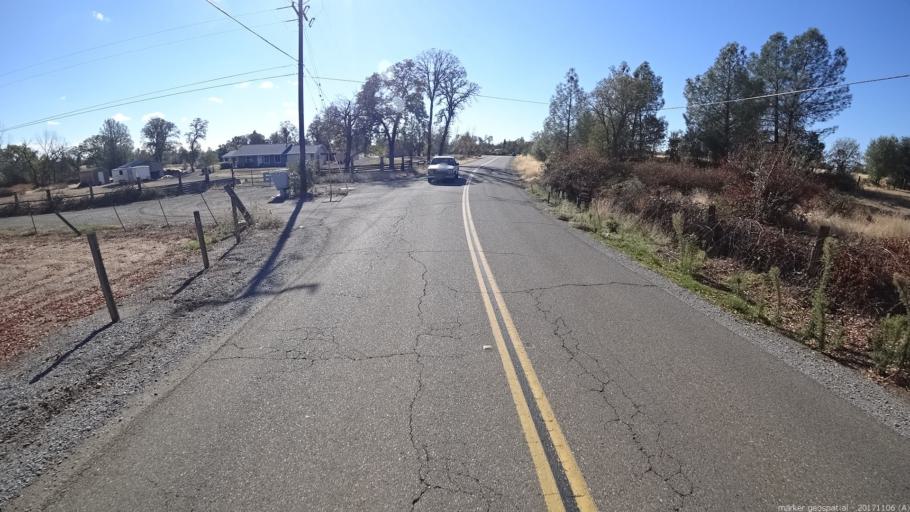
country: US
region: California
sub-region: Shasta County
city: Bella Vista
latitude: 40.6073
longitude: -122.2775
